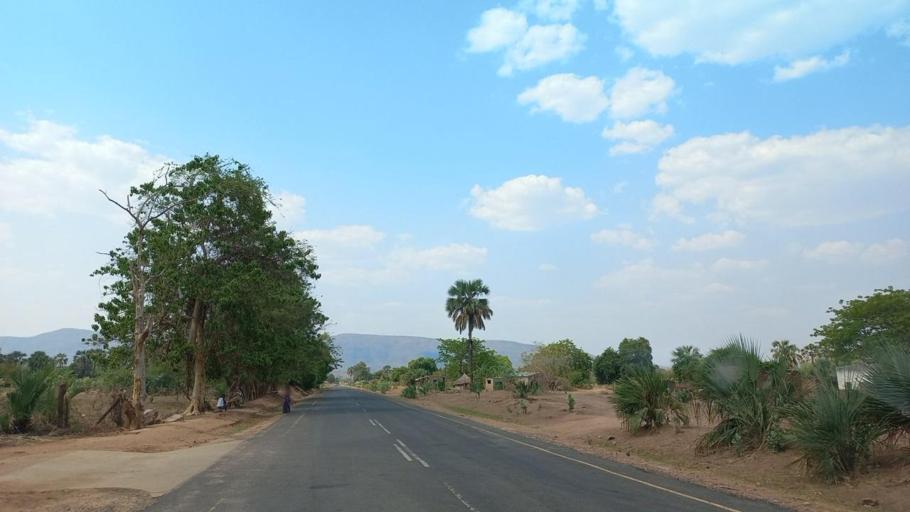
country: ZM
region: Lusaka
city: Luangwa
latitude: -15.0884
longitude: 30.1929
